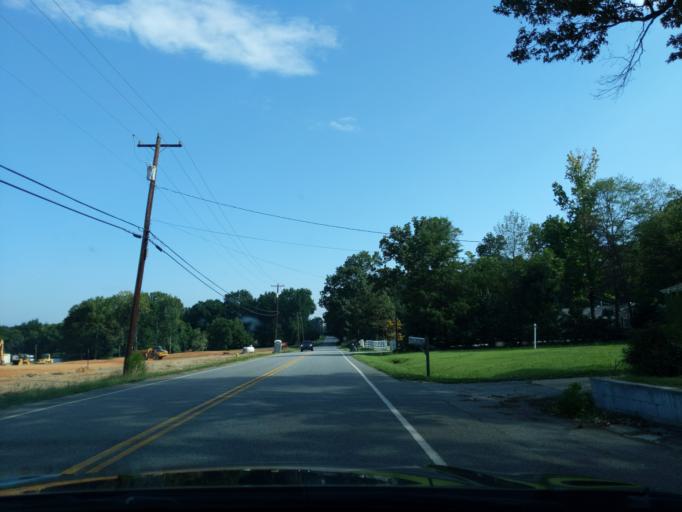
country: US
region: South Carolina
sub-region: Greenville County
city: Mauldin
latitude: 34.8108
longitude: -82.3111
